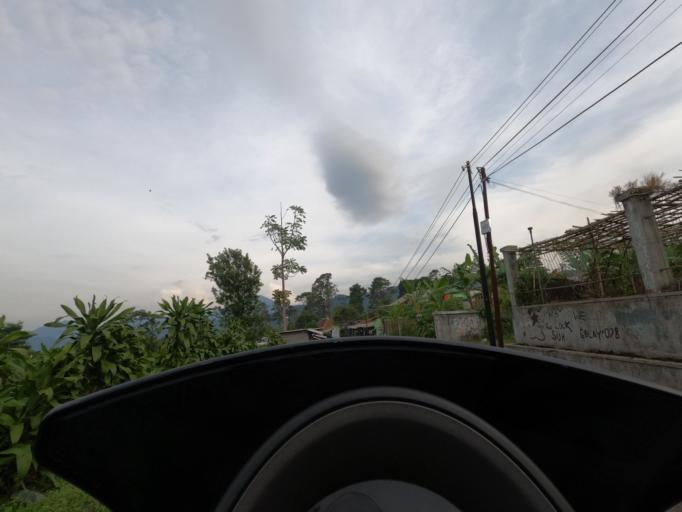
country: ID
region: West Java
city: Lembang
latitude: -6.7324
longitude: 107.6497
